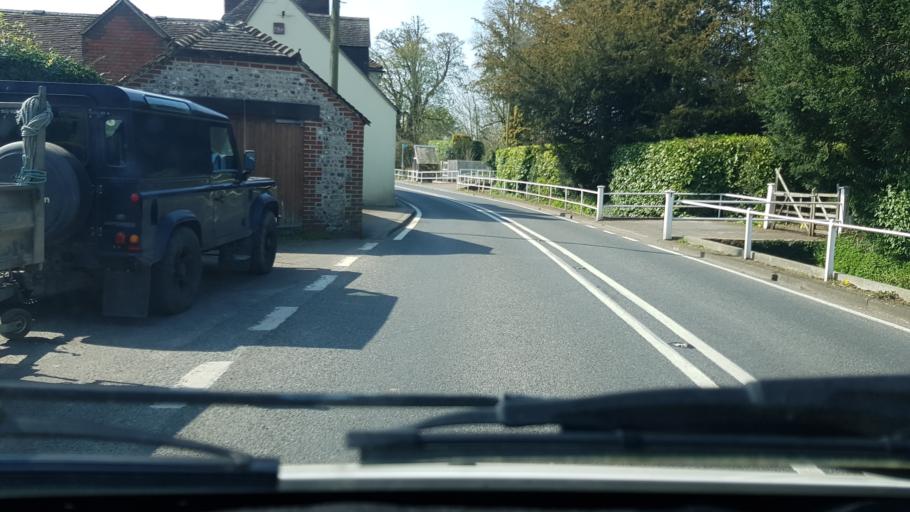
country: GB
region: England
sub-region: West Sussex
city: Boxgrove
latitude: 50.9116
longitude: -0.7536
